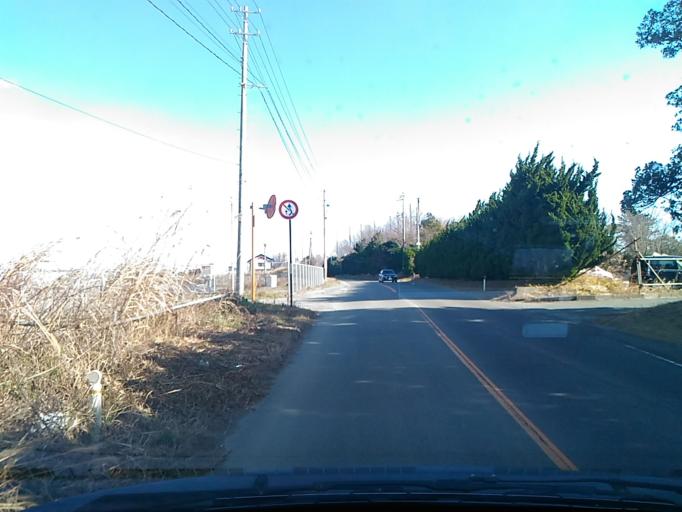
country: JP
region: Fukushima
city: Iwaki
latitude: 36.9181
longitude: 140.8444
